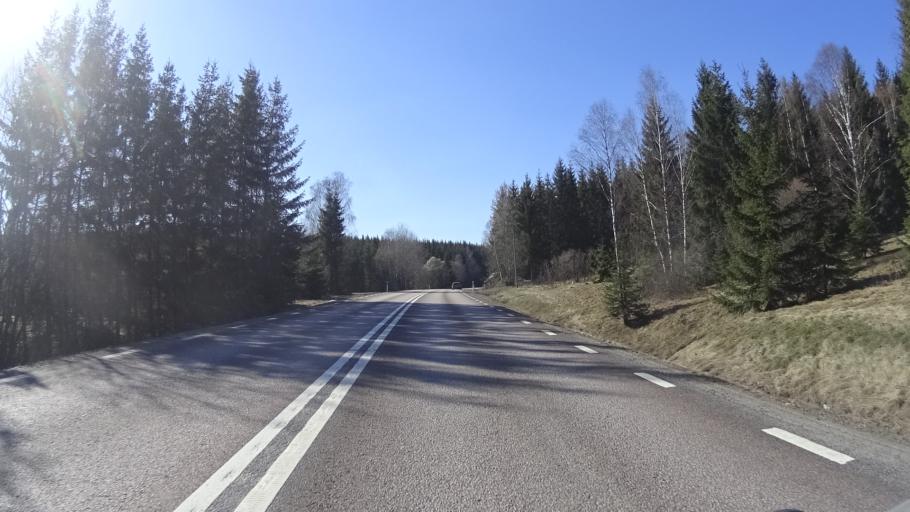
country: SE
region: Vaermland
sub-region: Karlstads Kommun
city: Edsvalla
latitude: 59.5235
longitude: 13.1491
